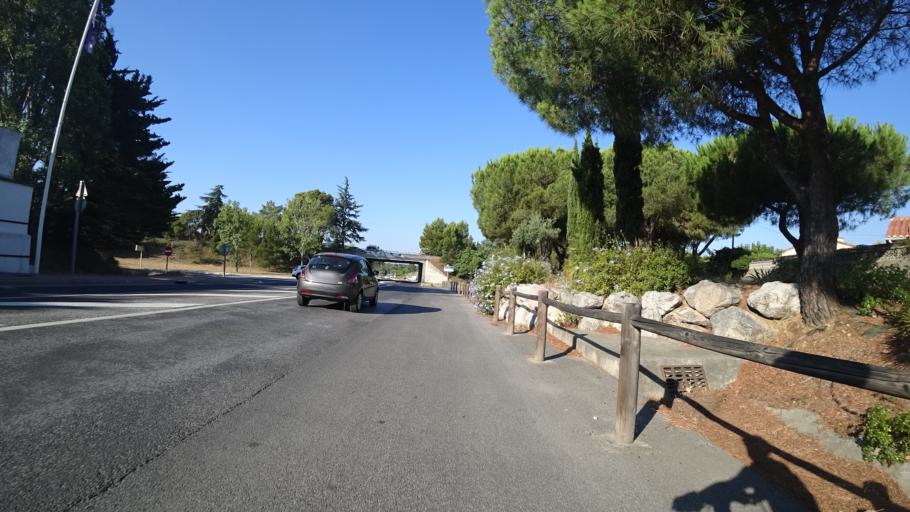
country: FR
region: Languedoc-Roussillon
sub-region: Departement des Pyrenees-Orientales
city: Canet-en-Roussillon
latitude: 42.7033
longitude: 3.0032
